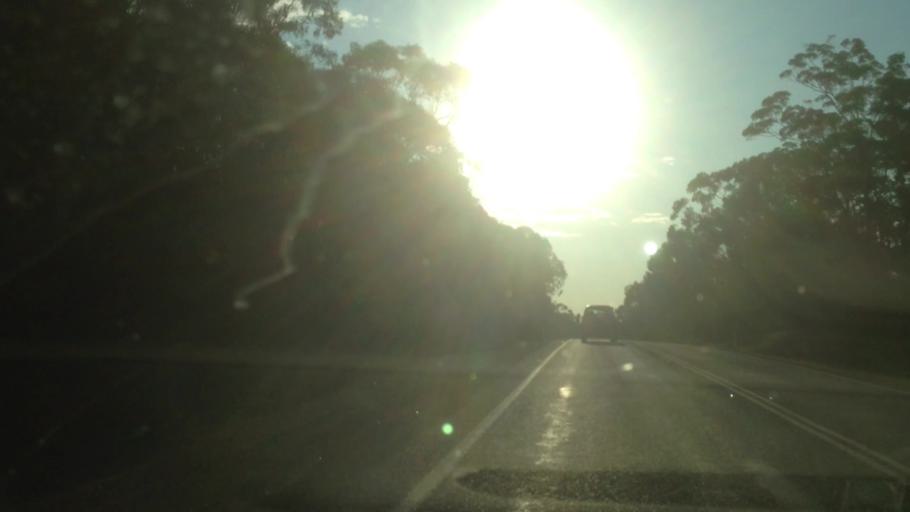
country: AU
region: New South Wales
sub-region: Cessnock
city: Kurri Kurri
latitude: -32.8300
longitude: 151.5039
